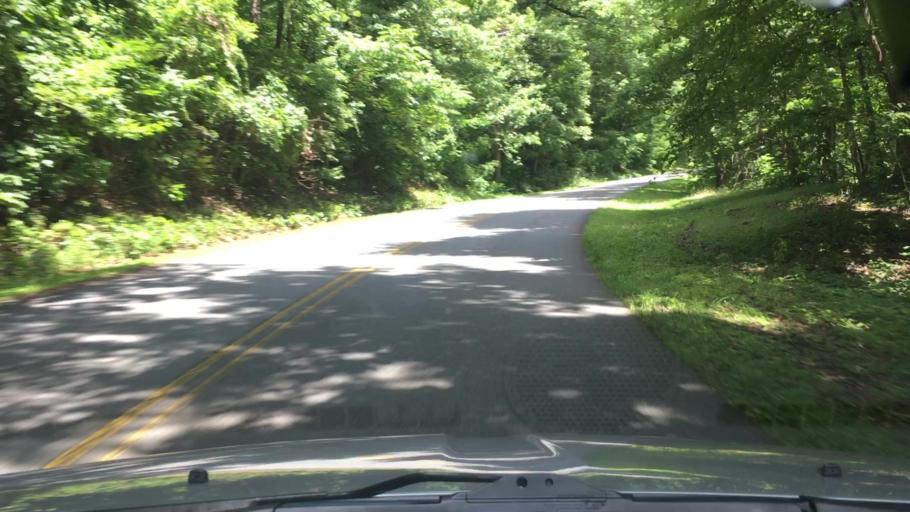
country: US
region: North Carolina
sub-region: Buncombe County
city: Asheville
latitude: 35.6335
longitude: -82.4962
